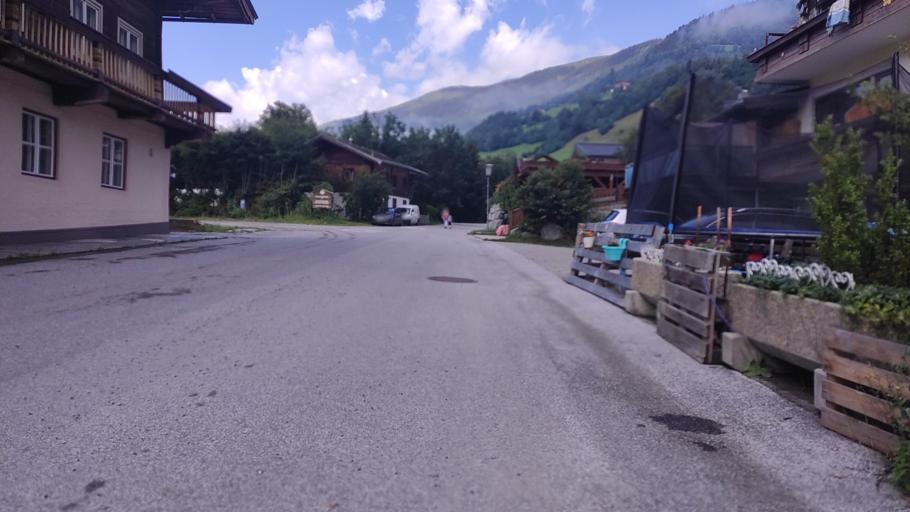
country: AT
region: Salzburg
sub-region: Politischer Bezirk Zell am See
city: Bramberg am Wildkogel
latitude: 47.2795
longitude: 12.3763
